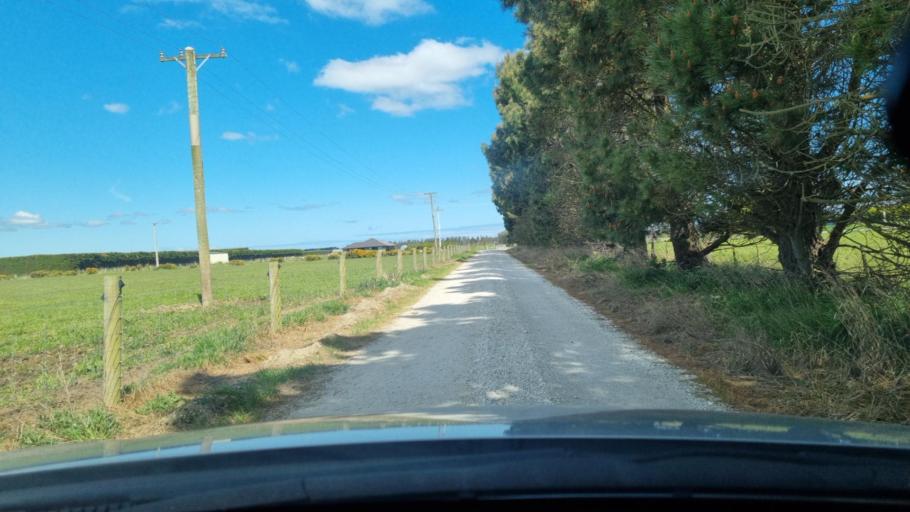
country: NZ
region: Southland
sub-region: Invercargill City
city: Invercargill
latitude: -46.3680
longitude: 168.2828
